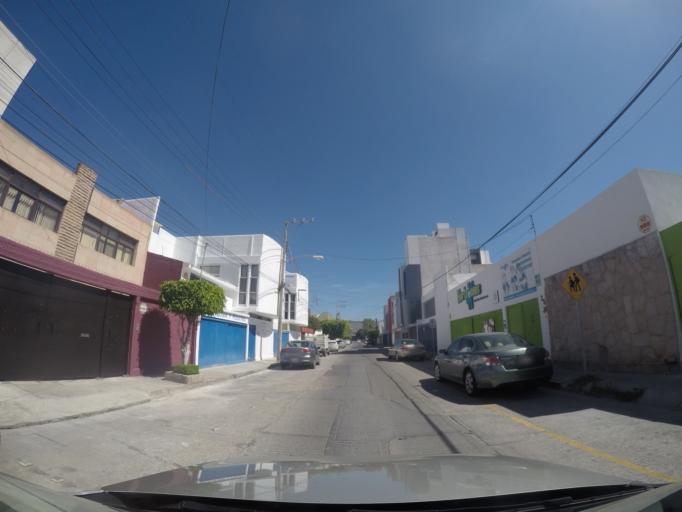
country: MX
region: San Luis Potosi
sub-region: San Luis Potosi
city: San Luis Potosi
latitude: 22.1521
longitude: -101.0069
